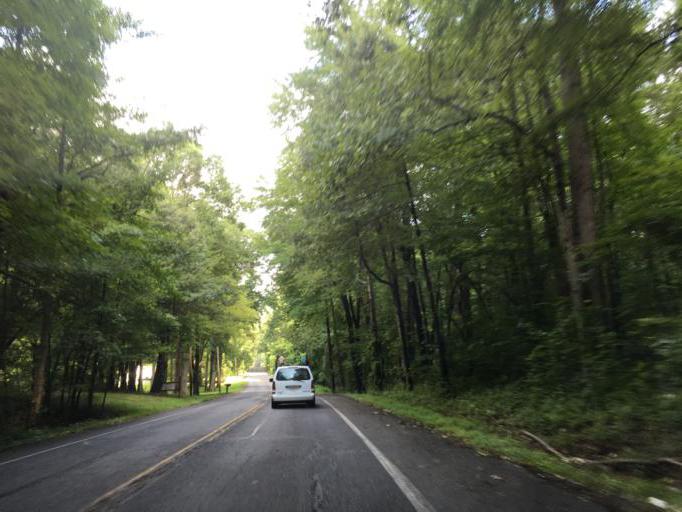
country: US
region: Maryland
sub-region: Anne Arundel County
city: Crownsville
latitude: 39.0101
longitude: -76.5957
